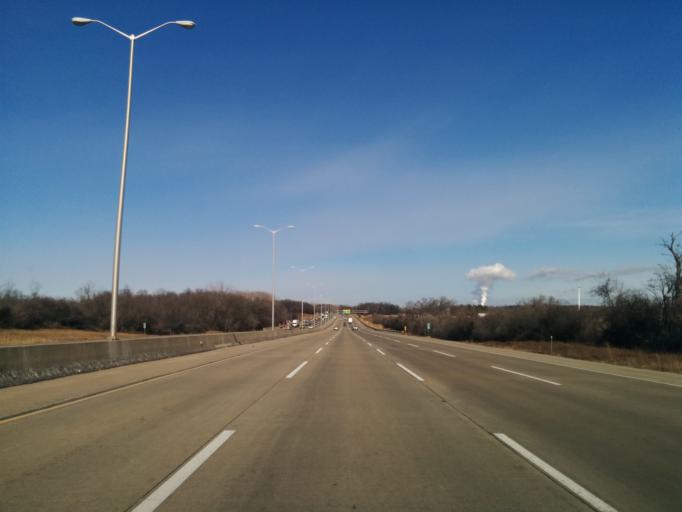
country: US
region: Illinois
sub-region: Lake County
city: Wadsworth
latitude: 42.4151
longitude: -87.9478
